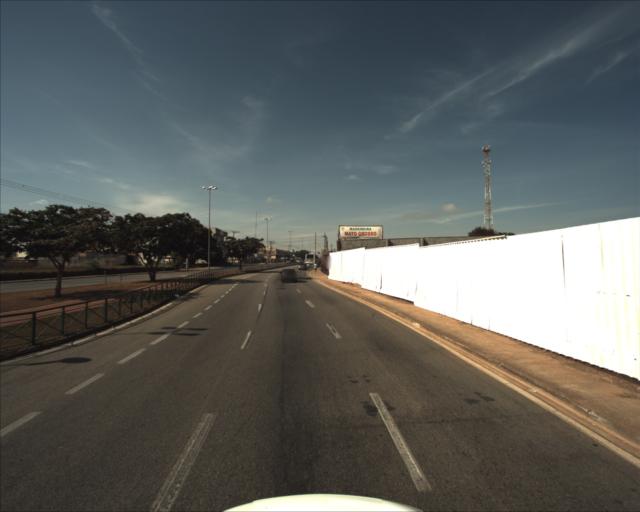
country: BR
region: Sao Paulo
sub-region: Sorocaba
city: Sorocaba
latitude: -23.4637
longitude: -47.4976
